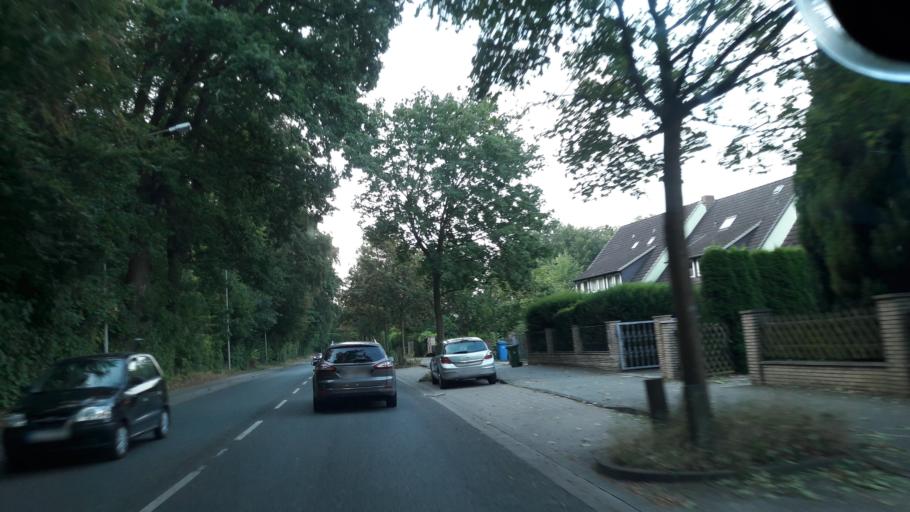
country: DE
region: Lower Saxony
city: Hildesheim
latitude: 52.1362
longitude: 9.9292
